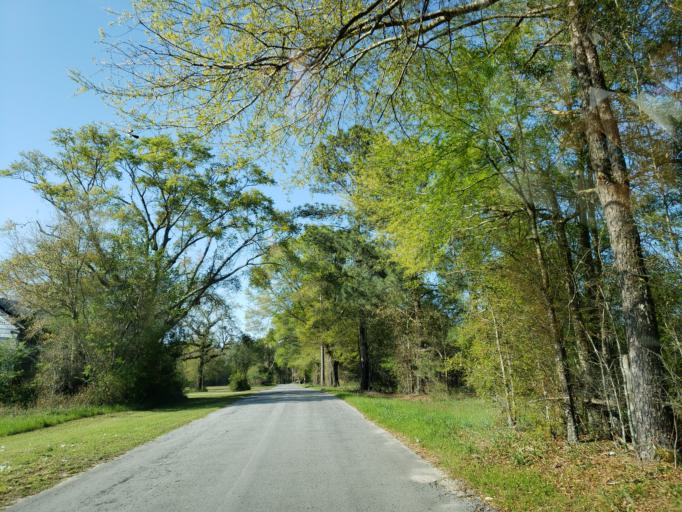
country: US
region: Mississippi
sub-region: Smith County
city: Taylorsville
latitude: 31.6964
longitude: -89.4136
